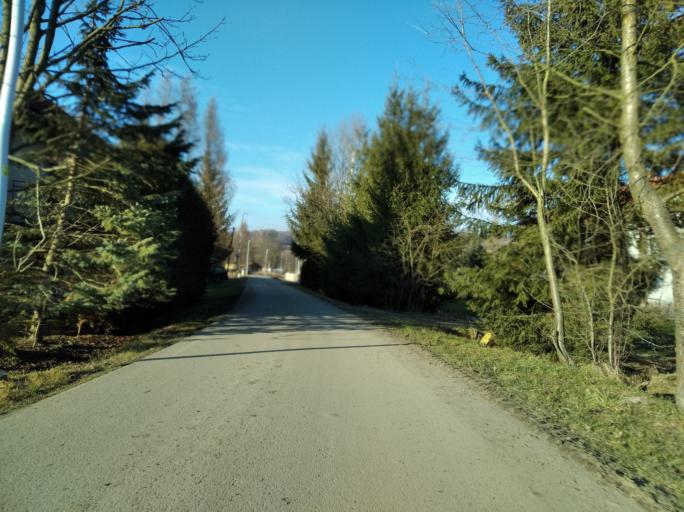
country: PL
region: Subcarpathian Voivodeship
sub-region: Powiat strzyzowski
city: Strzyzow
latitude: 49.8347
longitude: 21.8354
